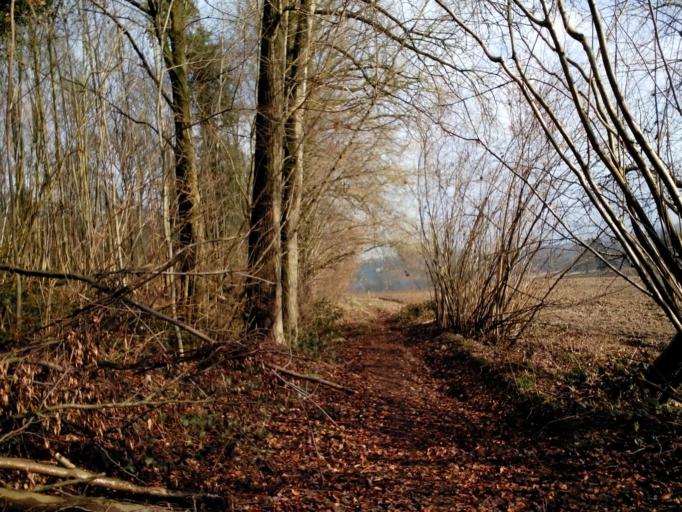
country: BE
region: Wallonia
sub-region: Province du Brabant Wallon
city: Grez-Doiceau
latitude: 50.7486
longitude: 4.6530
